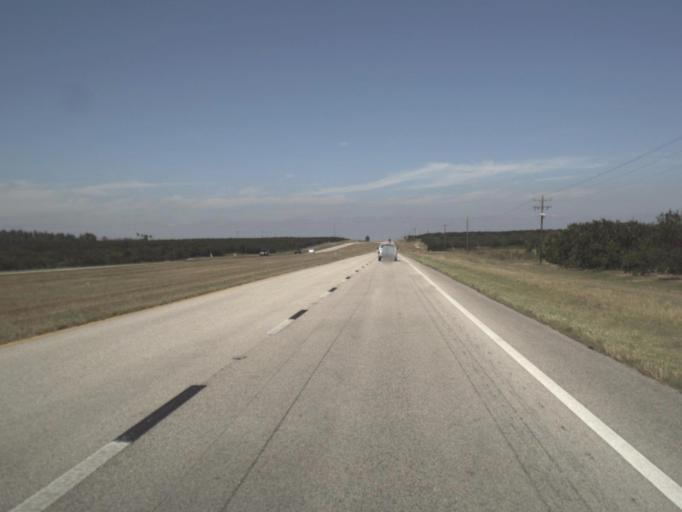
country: US
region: Florida
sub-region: Highlands County
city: Placid Lakes
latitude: 27.1723
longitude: -81.3286
